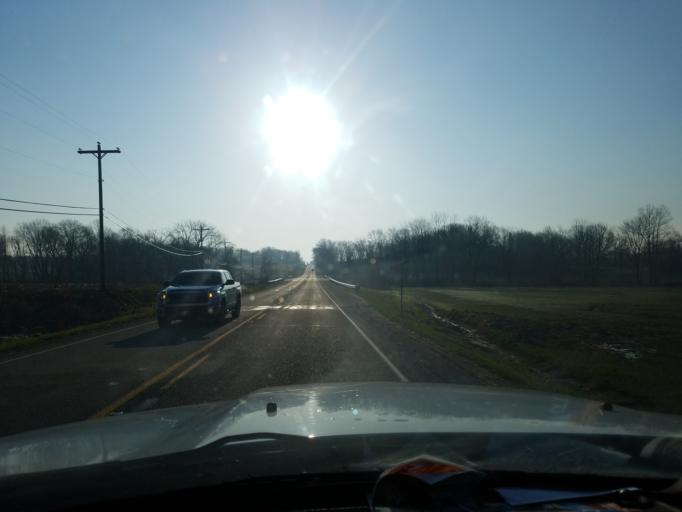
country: US
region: Indiana
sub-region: Vigo County
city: Seelyville
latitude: 39.3901
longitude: -87.2333
